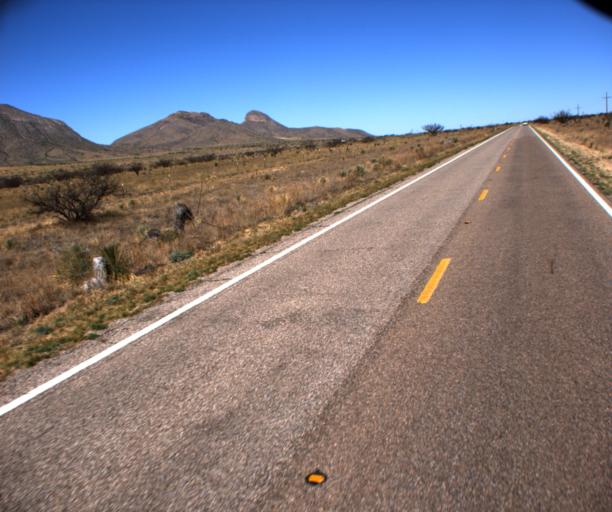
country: US
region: Arizona
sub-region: Cochise County
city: Huachuca City
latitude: 31.7031
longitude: -110.4344
